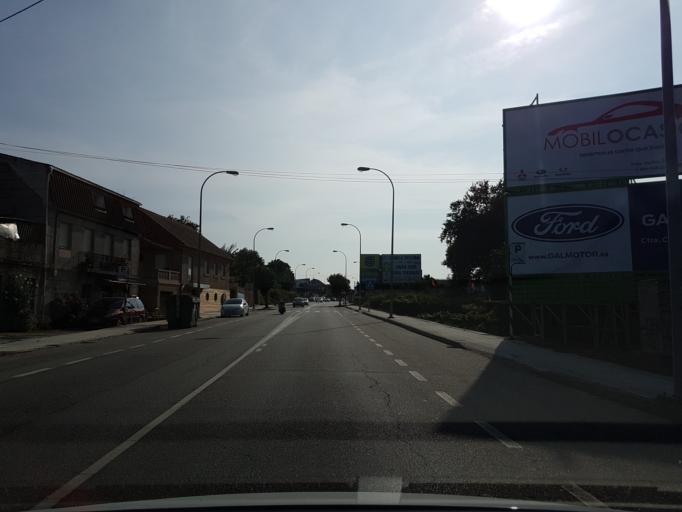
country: ES
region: Galicia
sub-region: Provincia de Pontevedra
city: Vigo
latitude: 42.2022
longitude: -8.7547
